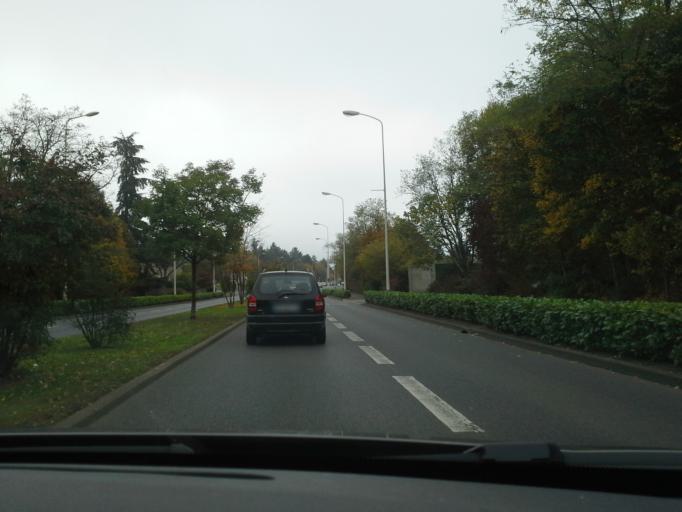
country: FR
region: Centre
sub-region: Departement d'Indre-et-Loire
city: Tours
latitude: 47.4110
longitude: 0.7029
